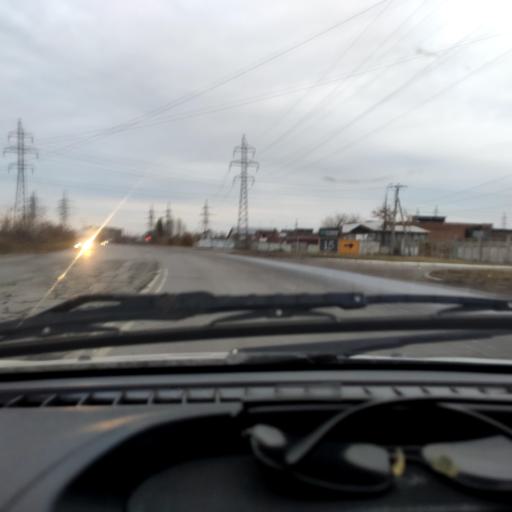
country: RU
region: Samara
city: Zhigulevsk
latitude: 53.5162
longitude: 49.4658
